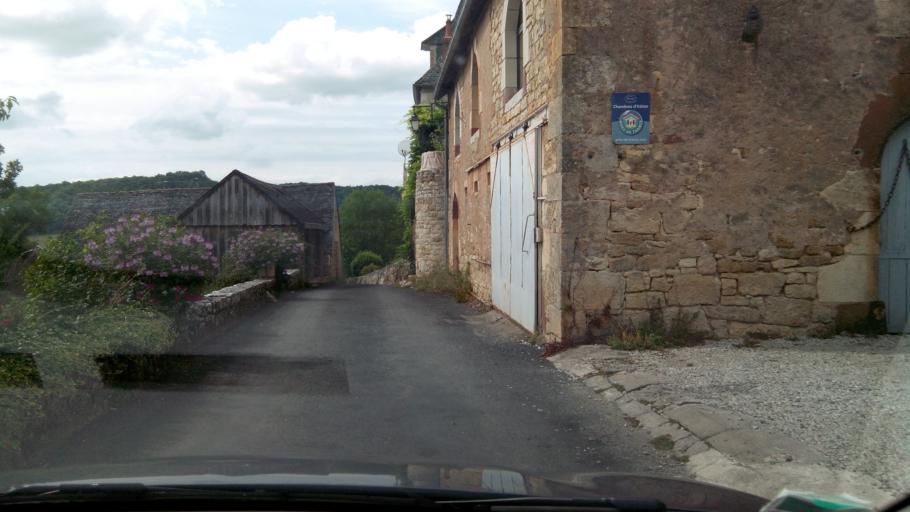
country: FR
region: Limousin
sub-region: Departement de la Correze
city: Cosnac
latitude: 45.0544
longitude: 1.5819
